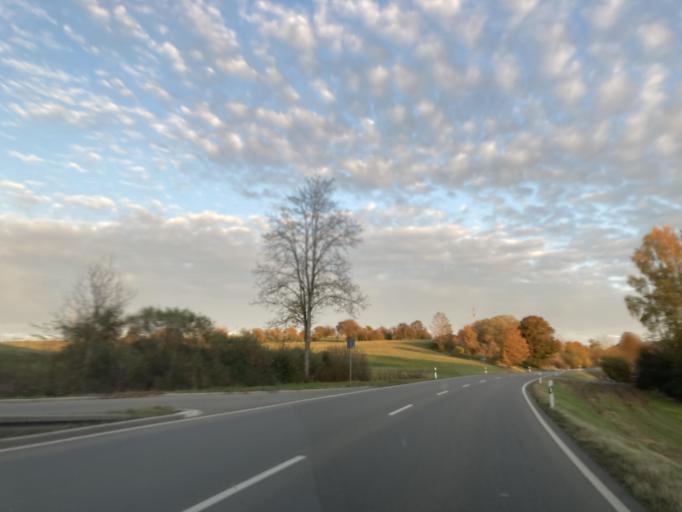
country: DE
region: Baden-Wuerttemberg
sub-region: Tuebingen Region
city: Schomberg
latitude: 48.2079
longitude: 8.7420
